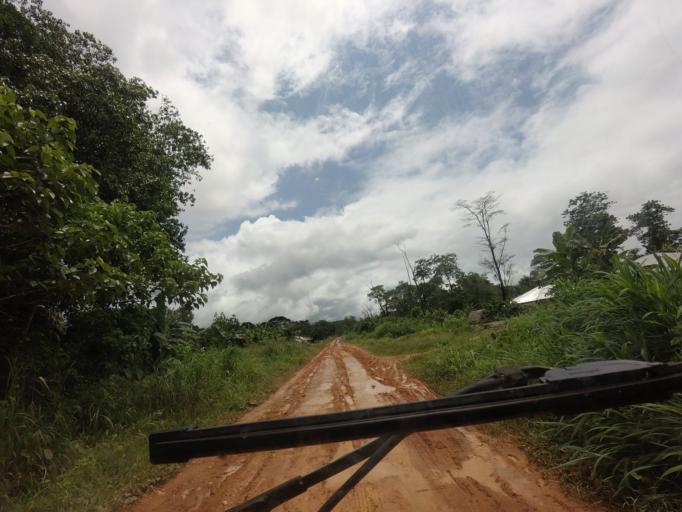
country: SL
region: Eastern Province
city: Tombodu
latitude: 8.1343
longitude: -10.6548
